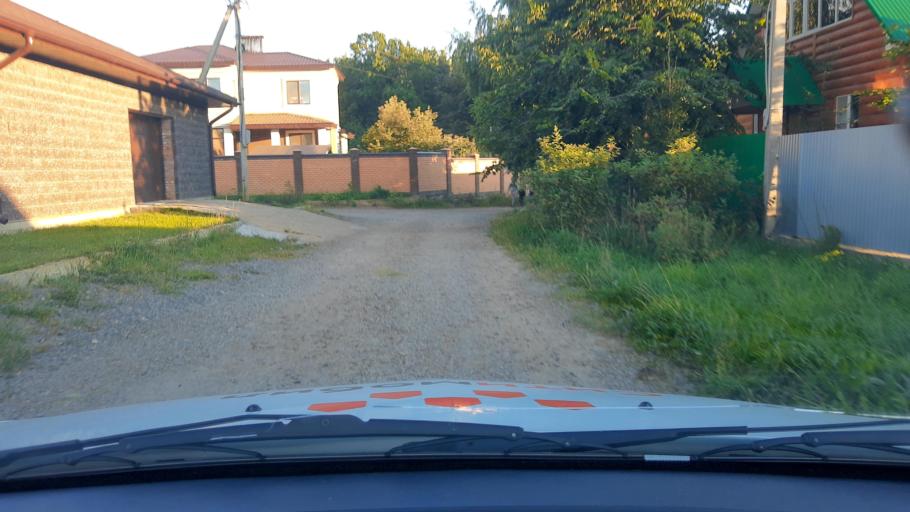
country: RU
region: Bashkortostan
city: Ufa
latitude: 54.6538
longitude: 56.0511
